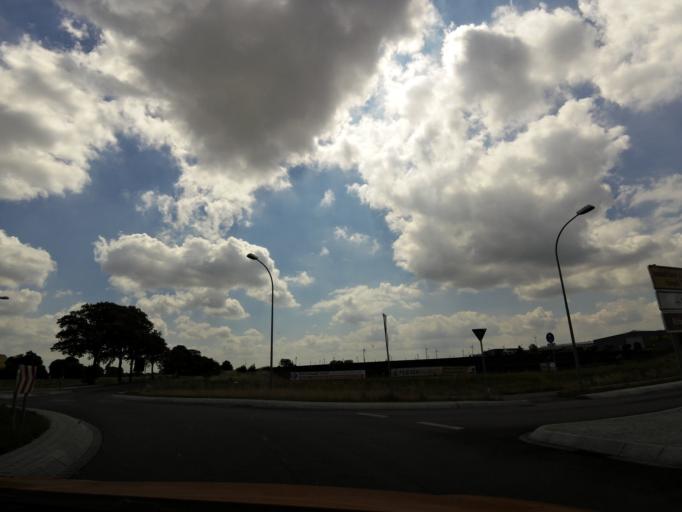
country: DE
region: Brandenburg
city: Wusterhausen
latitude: 52.8774
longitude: 12.4699
